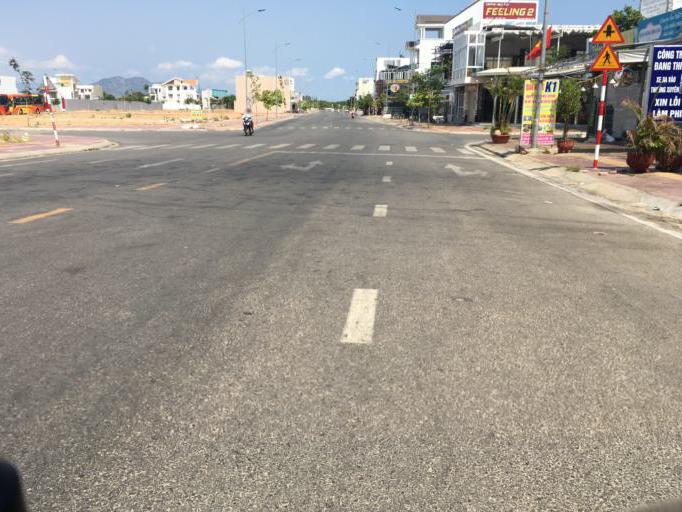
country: VN
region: Ninh Thuan
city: Phan Rang-Thap Cham
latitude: 11.5701
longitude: 108.9950
